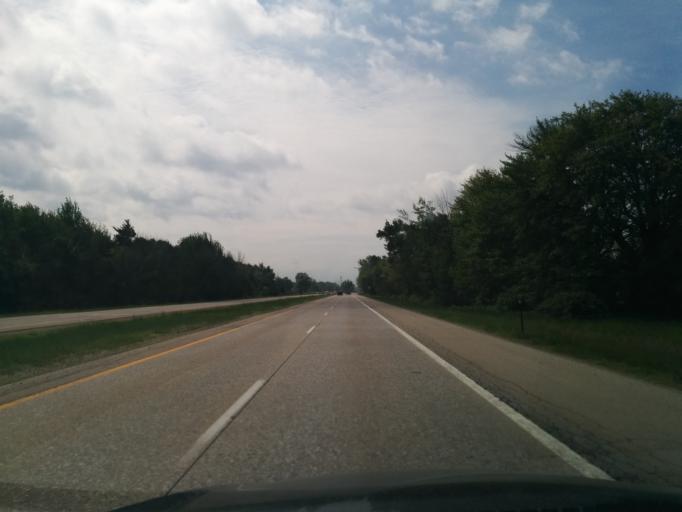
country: US
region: Michigan
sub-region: Ottawa County
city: Grand Haven
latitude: 43.0135
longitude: -86.2084
